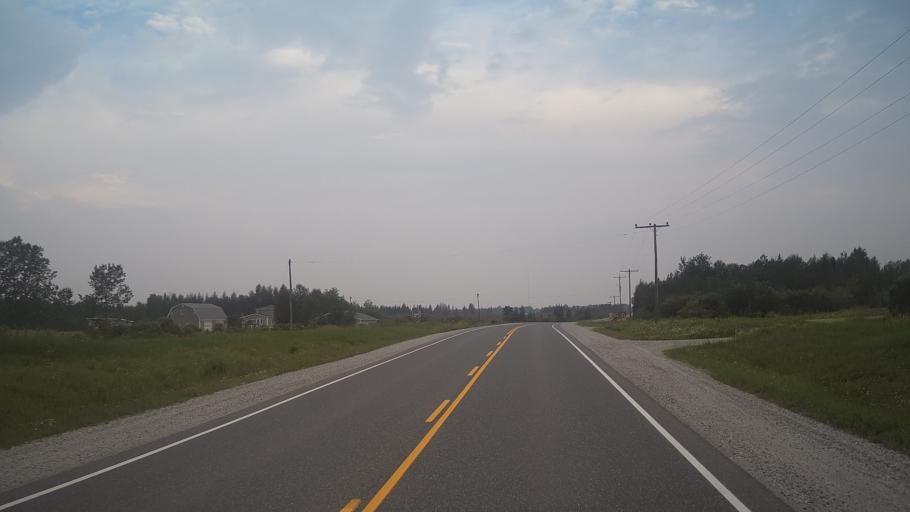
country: CA
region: Ontario
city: Hearst
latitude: 49.6610
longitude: -83.4806
